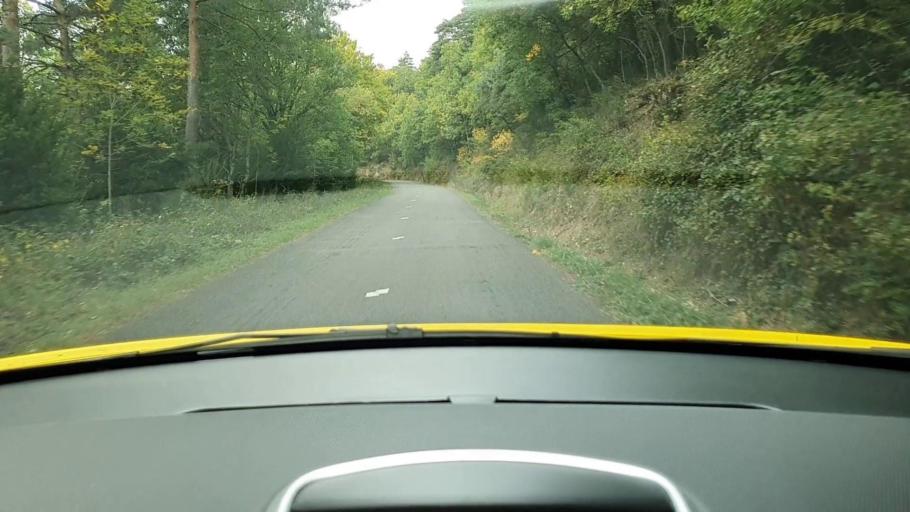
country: FR
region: Languedoc-Roussillon
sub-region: Departement de la Lozere
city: Meyrueis
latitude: 44.0789
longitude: 3.4157
